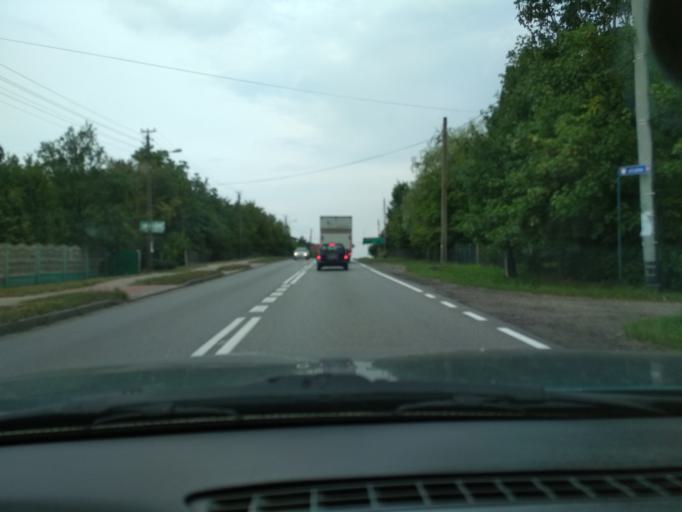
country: PL
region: Silesian Voivodeship
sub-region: Powiat zawiercianski
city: Wysoka
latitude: 50.4454
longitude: 19.3622
